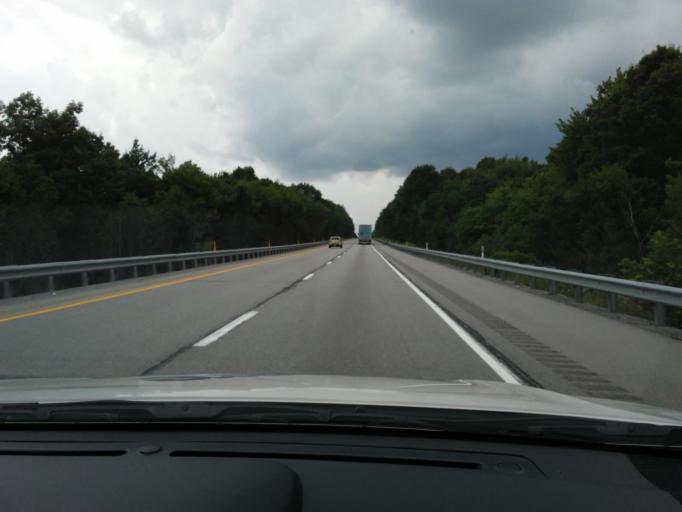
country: US
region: Pennsylvania
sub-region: Clearfield County
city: Troy
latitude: 40.9896
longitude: -78.2006
